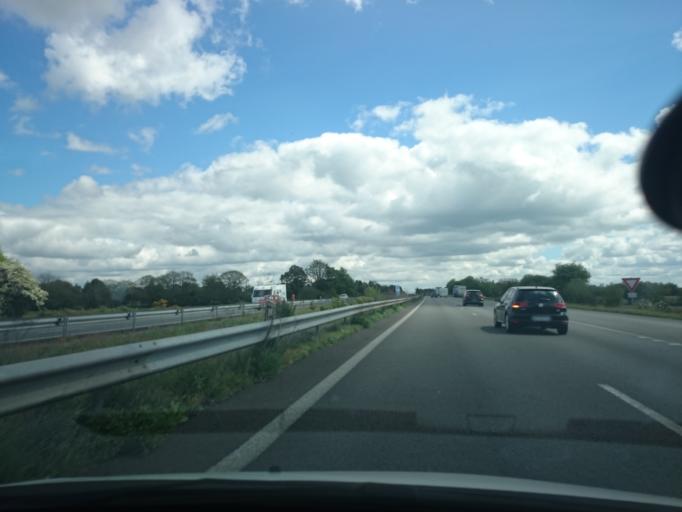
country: FR
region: Pays de la Loire
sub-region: Departement de la Loire-Atlantique
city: Le Temple-de-Bretagne
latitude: 47.3106
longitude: -1.7662
